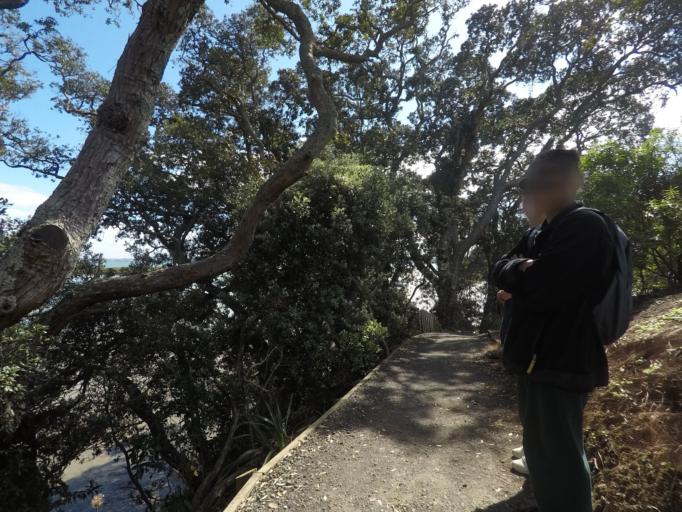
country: NZ
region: Auckland
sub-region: Auckland
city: Rosebank
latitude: -36.8544
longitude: 174.7127
